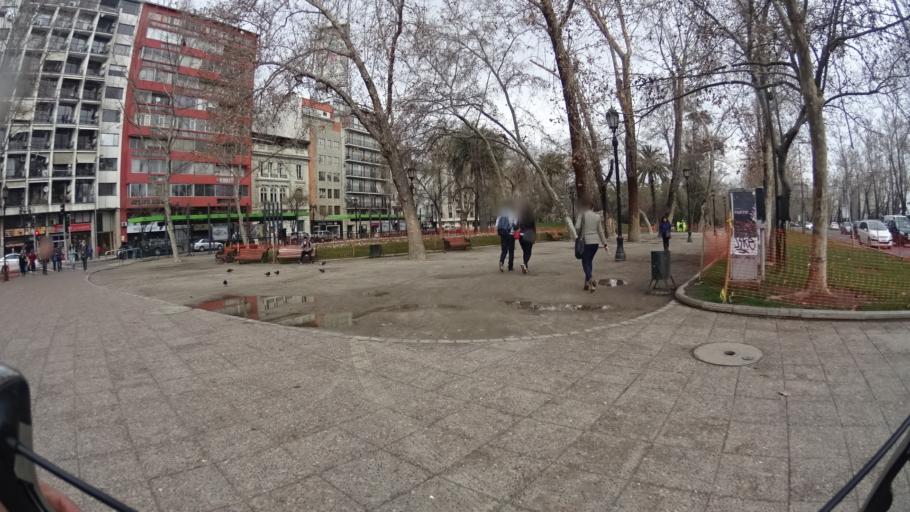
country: CL
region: Santiago Metropolitan
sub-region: Provincia de Santiago
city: Santiago
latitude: -33.4365
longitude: -70.6355
